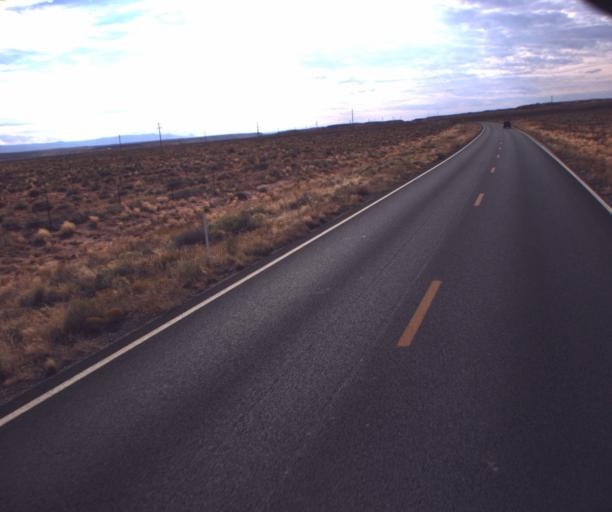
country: US
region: Arizona
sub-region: Apache County
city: Many Farms
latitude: 36.6163
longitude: -109.5800
